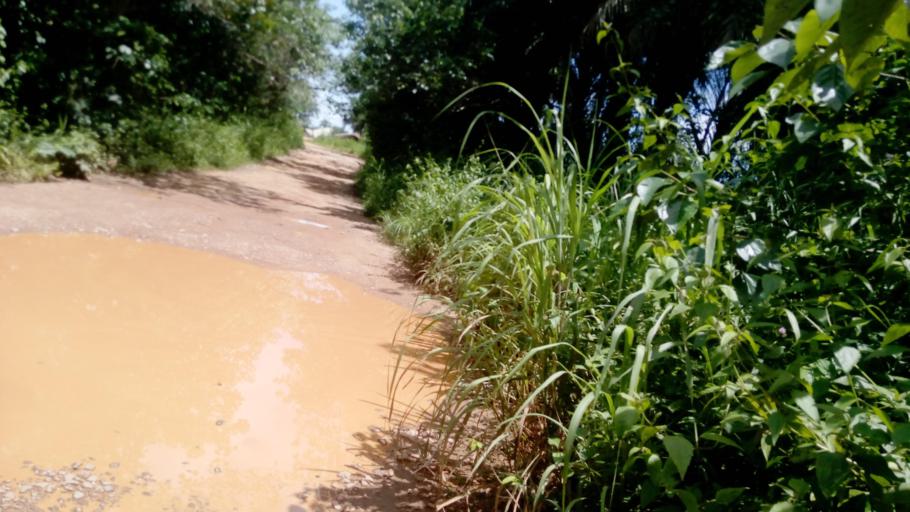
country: SL
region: Northern Province
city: Binkolo
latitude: 8.9534
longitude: -11.9728
